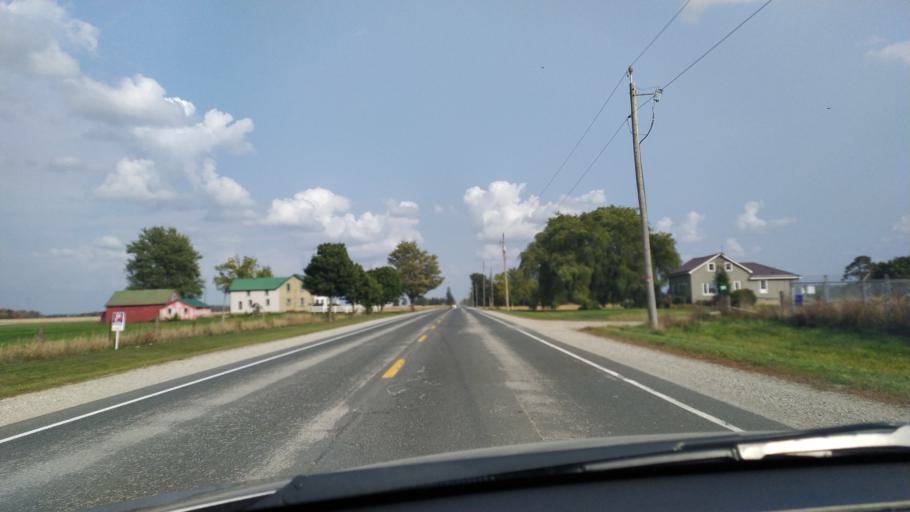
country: CA
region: Ontario
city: Stratford
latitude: 43.3514
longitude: -80.8641
